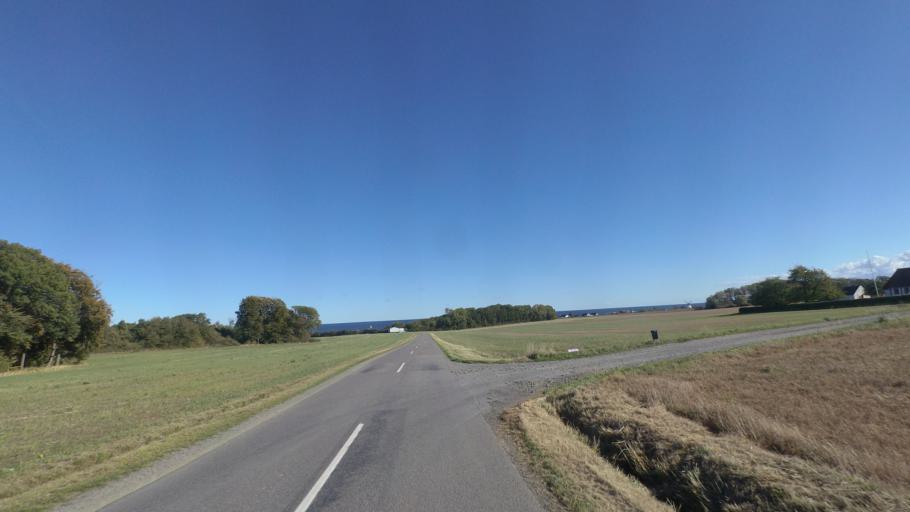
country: DK
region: Capital Region
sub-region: Bornholm Kommune
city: Nexo
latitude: 55.1107
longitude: 15.1310
